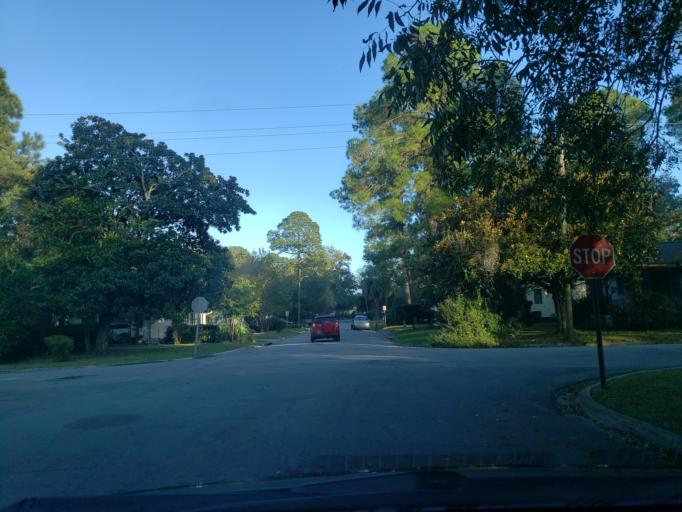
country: US
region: Georgia
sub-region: Chatham County
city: Thunderbolt
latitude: 32.0531
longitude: -81.0798
